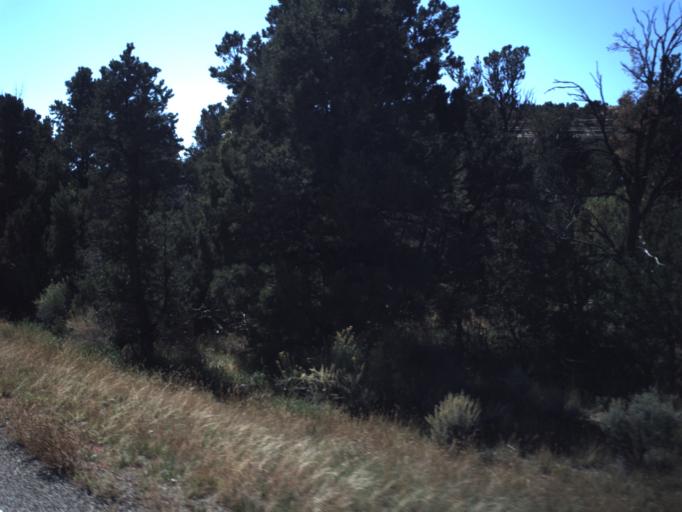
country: US
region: Utah
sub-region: Wayne County
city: Loa
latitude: 37.9233
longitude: -111.4259
